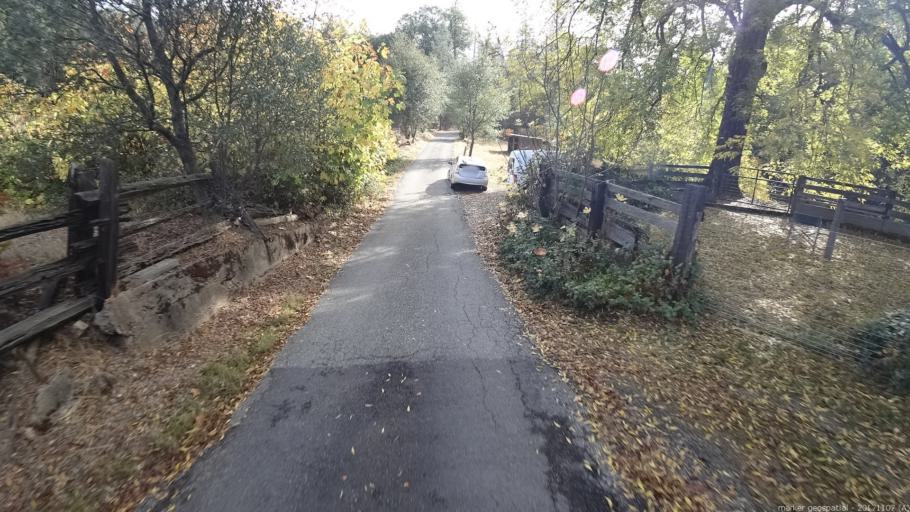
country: US
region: California
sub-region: Shasta County
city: Shasta
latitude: 40.5413
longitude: -122.5686
